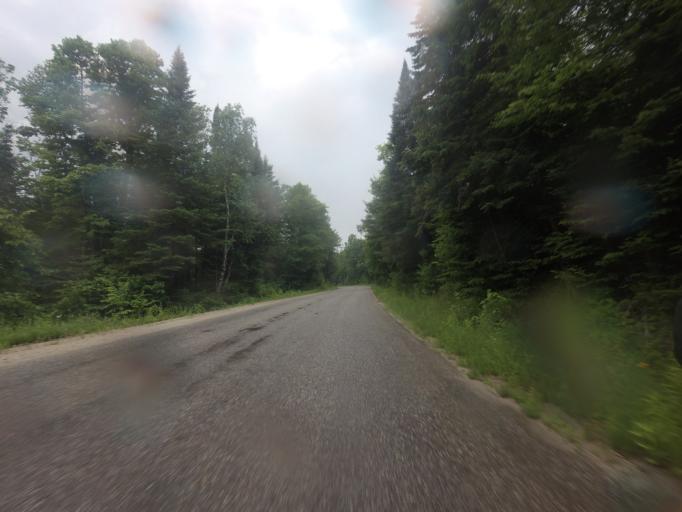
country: CA
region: Quebec
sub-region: Outaouais
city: Maniwaki
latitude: 46.4348
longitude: -75.9436
